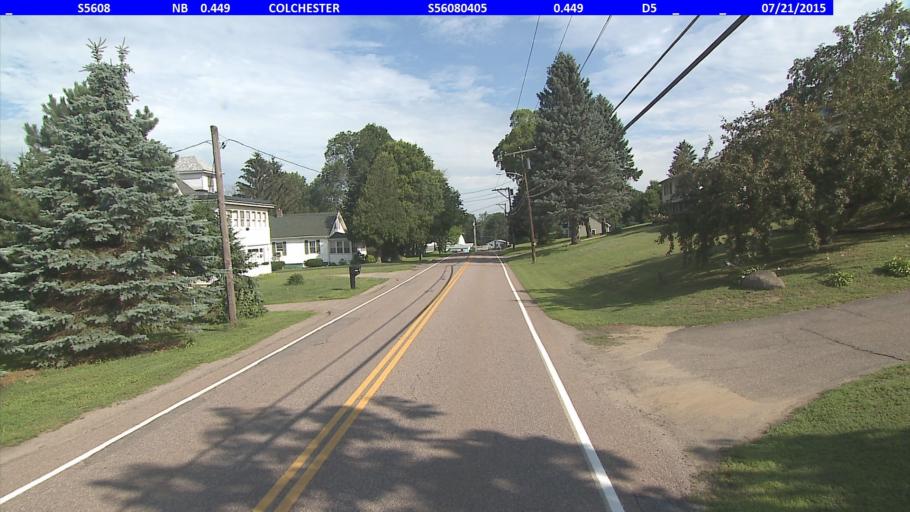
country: US
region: Vermont
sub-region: Chittenden County
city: Winooski
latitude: 44.5055
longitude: -73.2007
